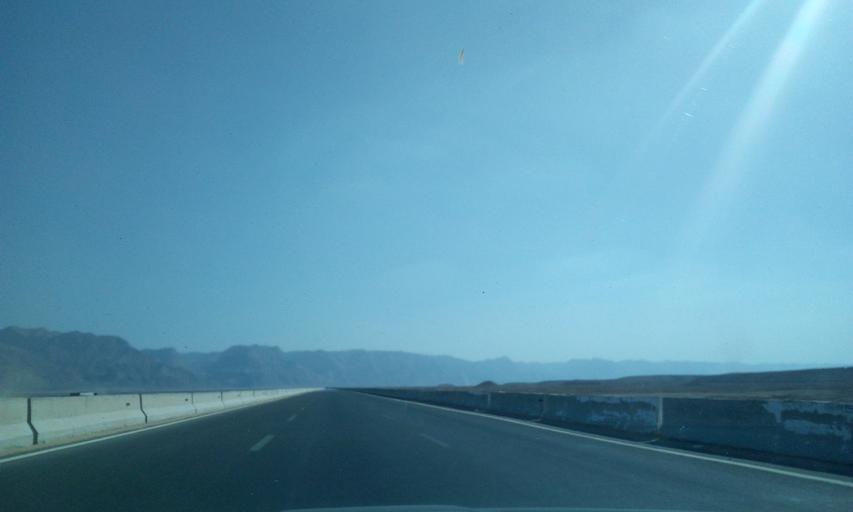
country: EG
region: As Suways
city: Ain Sukhna
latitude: 29.6018
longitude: 32.2081
